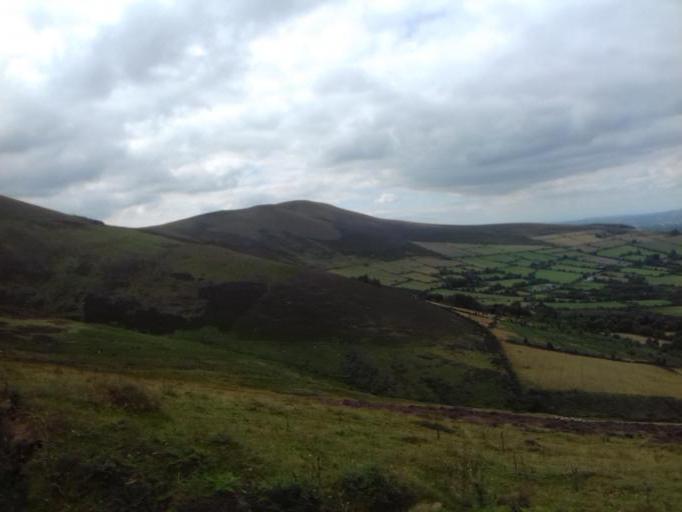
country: IE
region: Leinster
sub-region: Loch Garman
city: Bunclody
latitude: 52.6438
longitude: -6.7729
